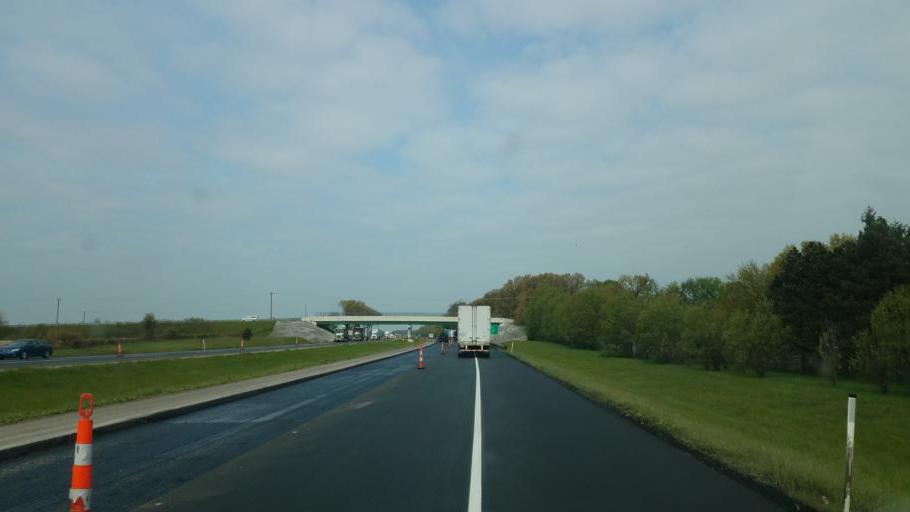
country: US
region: Indiana
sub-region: Saint Joseph County
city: Granger
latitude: 41.7338
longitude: -86.1079
